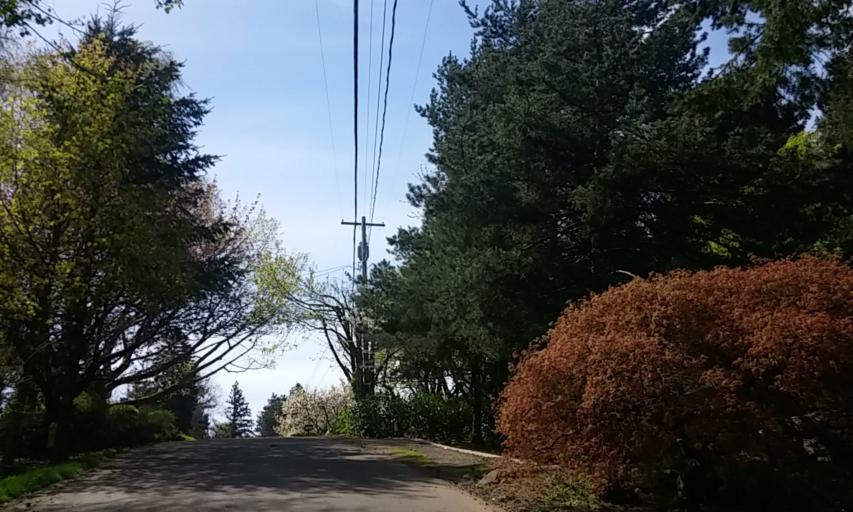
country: US
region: Oregon
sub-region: Washington County
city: West Haven-Sylvan
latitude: 45.5142
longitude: -122.7498
